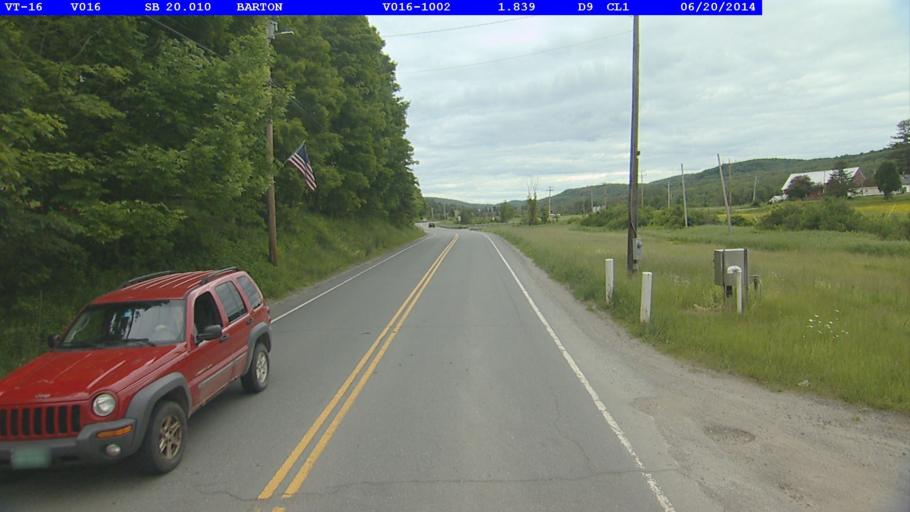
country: US
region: Vermont
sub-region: Orleans County
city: Newport
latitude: 44.7436
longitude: -72.1812
